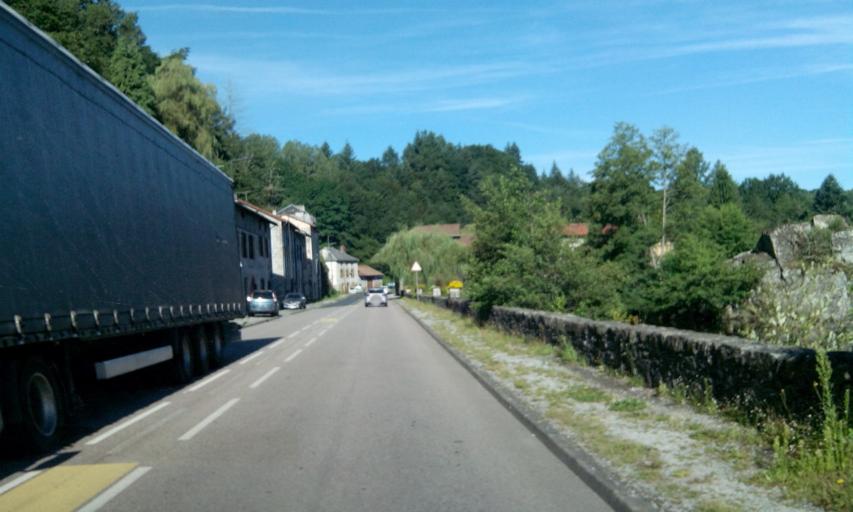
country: FR
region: Limousin
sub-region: Departement de la Haute-Vienne
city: Saint-Leonard-de-Noblat
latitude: 45.8343
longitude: 1.4756
